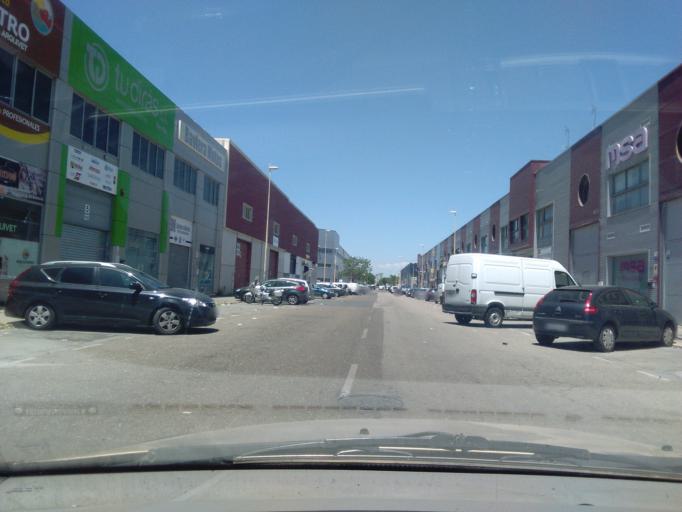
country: ES
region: Andalusia
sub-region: Provincia de Sevilla
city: Sevilla
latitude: 37.3809
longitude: -5.9303
